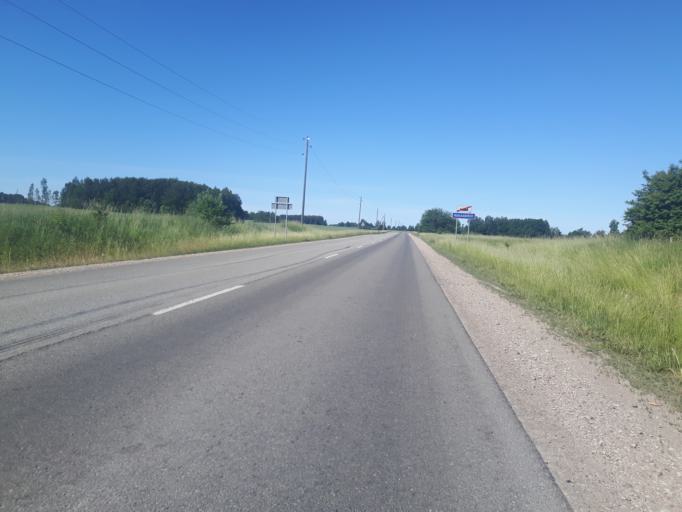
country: LV
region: Aizpute
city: Aizpute
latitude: 56.7117
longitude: 21.5528
